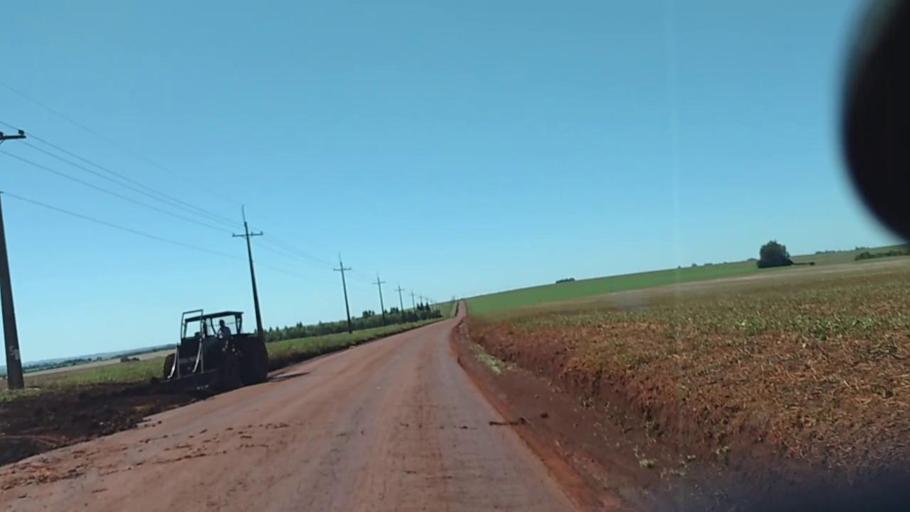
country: PY
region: Alto Parana
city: Naranjal
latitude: -25.9412
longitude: -55.2875
